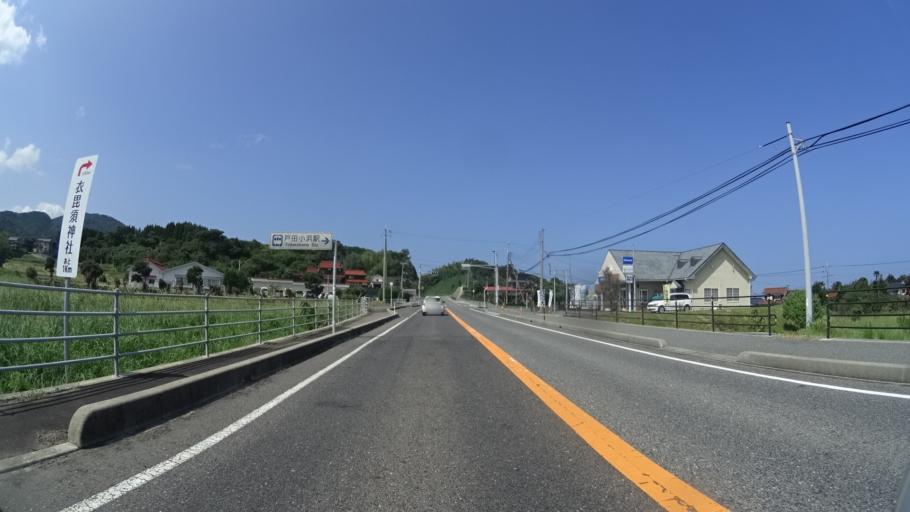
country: JP
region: Shimane
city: Masuda
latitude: 34.6713
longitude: 131.7399
